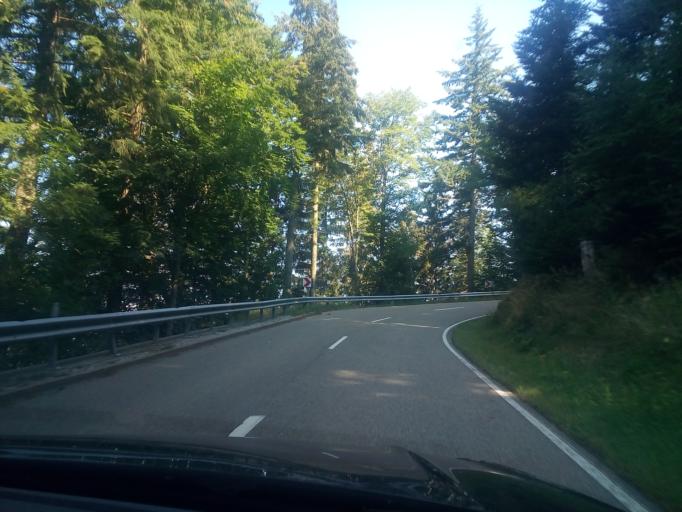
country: DE
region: Baden-Wuerttemberg
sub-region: Karlsruhe Region
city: Buhlertal
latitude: 48.6614
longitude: 8.2212
